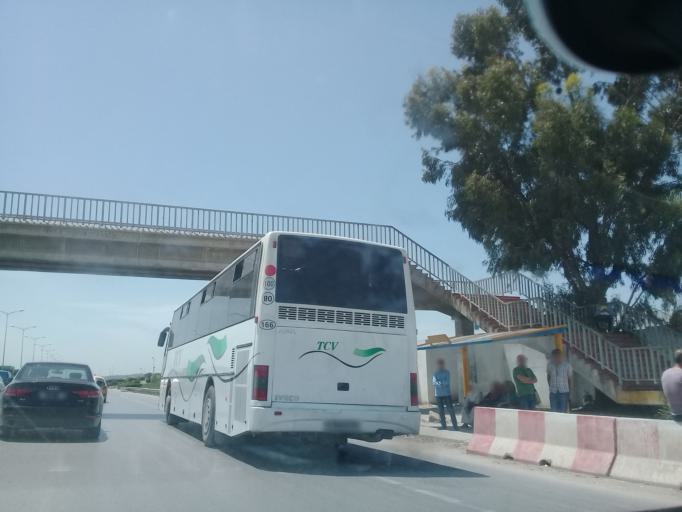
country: TN
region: Ariana
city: Ariana
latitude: 36.8381
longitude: 10.2324
